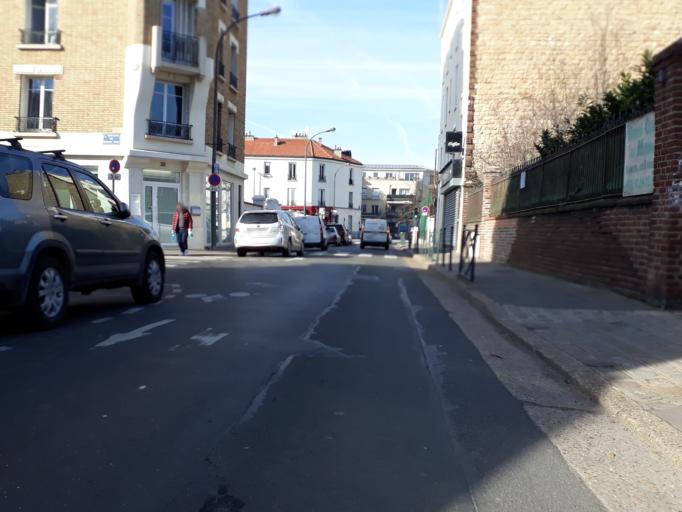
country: FR
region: Ile-de-France
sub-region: Departement des Hauts-de-Seine
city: Asnieres-sur-Seine
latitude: 48.9206
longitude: 2.2839
